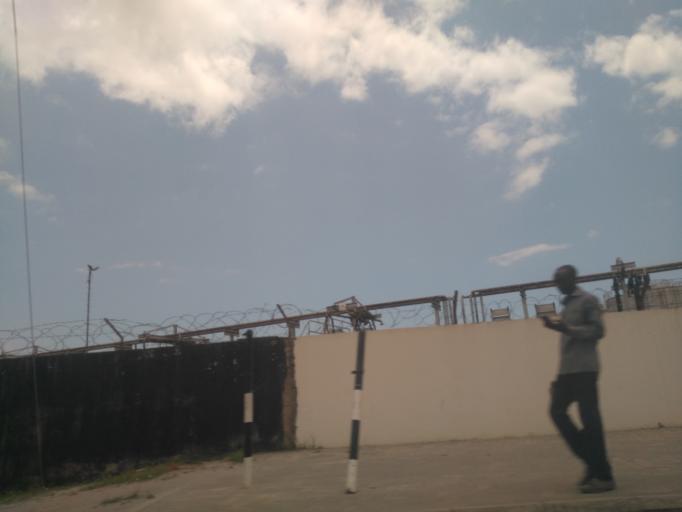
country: TZ
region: Dar es Salaam
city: Dar es Salaam
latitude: -6.8486
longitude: 39.2931
